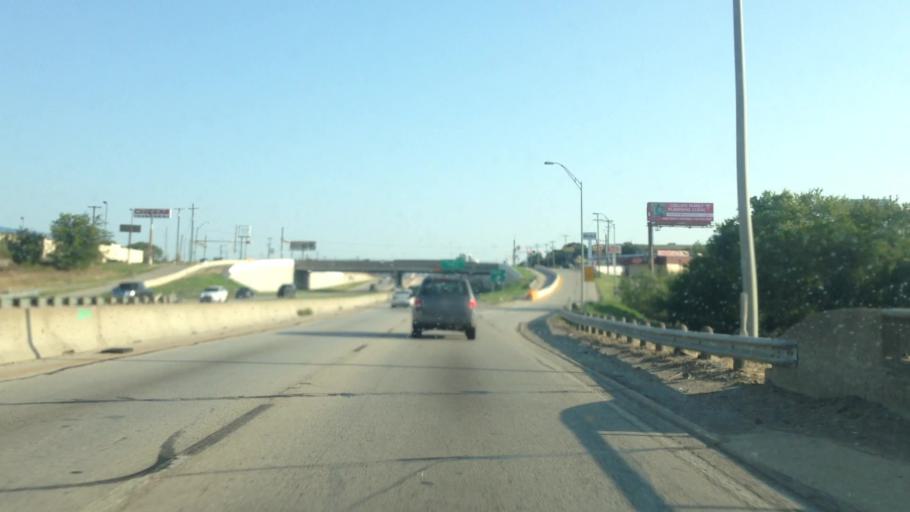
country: US
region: Texas
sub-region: Tarrant County
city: Richland Hills
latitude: 32.7807
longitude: -97.2128
